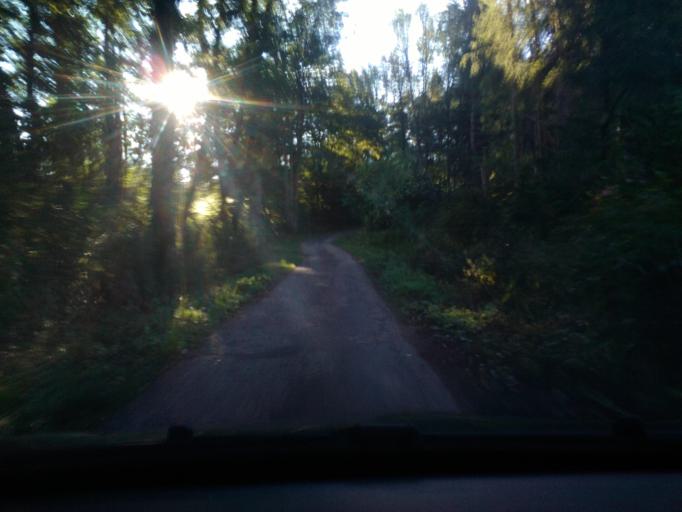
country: FR
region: Lorraine
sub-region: Departement des Vosges
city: Senones
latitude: 48.3761
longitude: 7.0300
